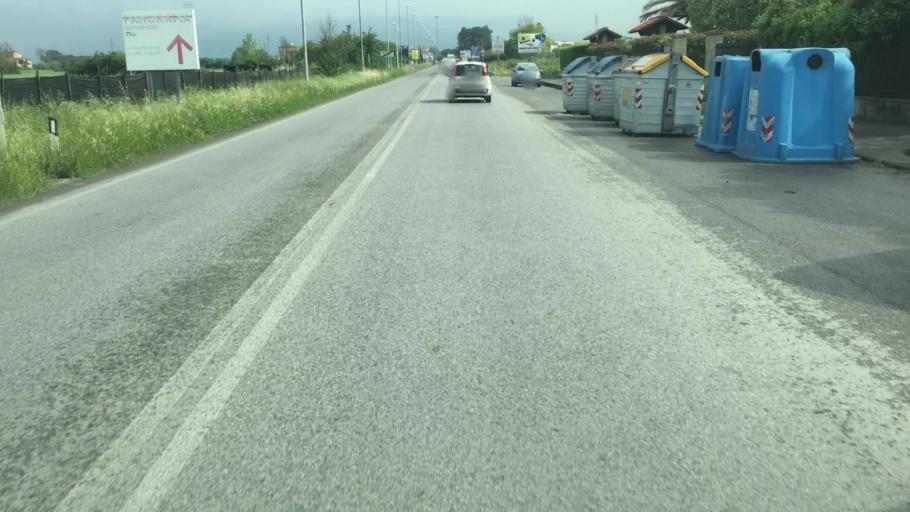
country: IT
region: Tuscany
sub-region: Province of Florence
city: San Mauro
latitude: 43.8095
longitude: 11.1181
